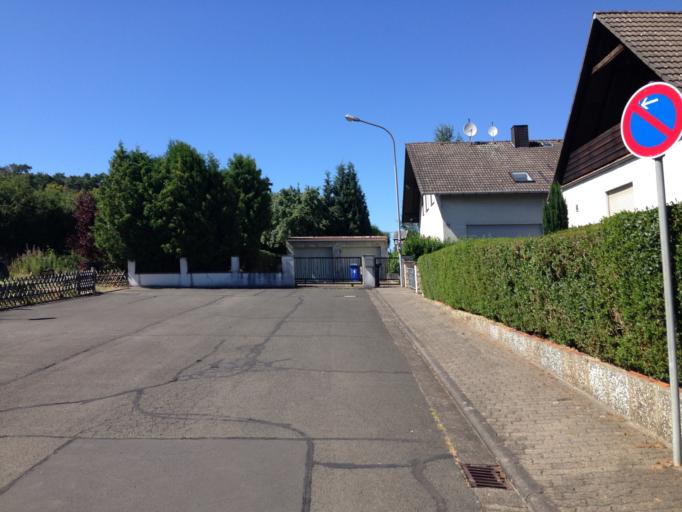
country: DE
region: Hesse
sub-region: Regierungsbezirk Giessen
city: Grossen Buseck
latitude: 50.5908
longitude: 8.7982
